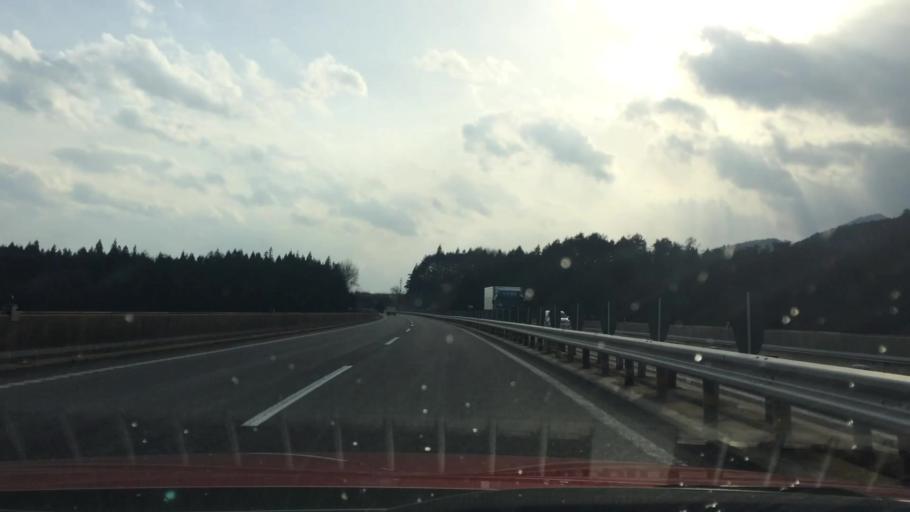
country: JP
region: Nagano
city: Ina
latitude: 35.6724
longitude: 137.9049
